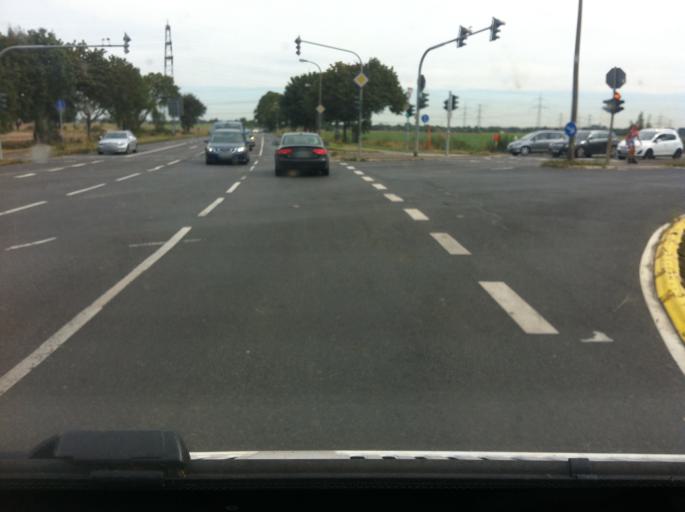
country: DE
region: North Rhine-Westphalia
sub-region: Regierungsbezirk Koln
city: Frechen
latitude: 50.9543
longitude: 6.8017
